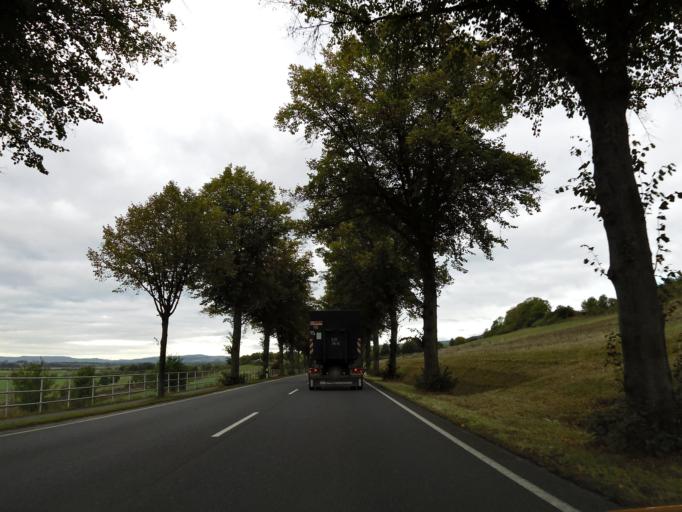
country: DE
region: Lower Saxony
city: Kreiensen
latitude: 51.7727
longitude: 9.9454
